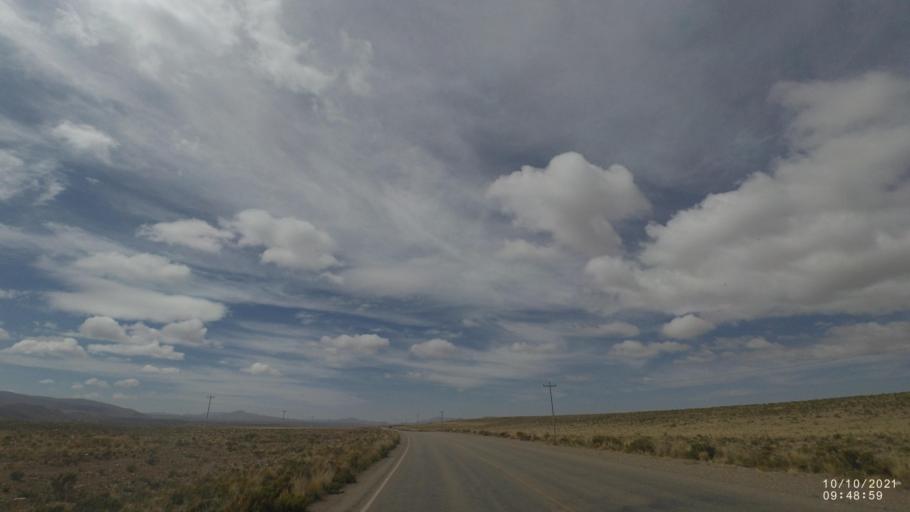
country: BO
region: La Paz
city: Quime
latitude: -17.2192
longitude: -67.3410
